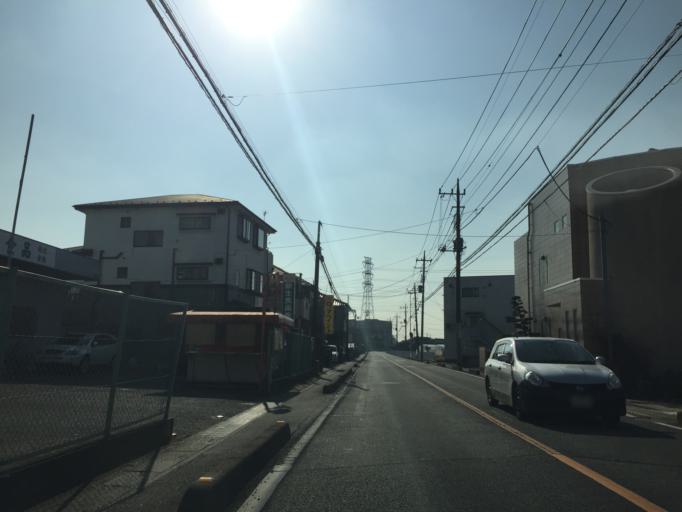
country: JP
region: Saitama
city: Shiki
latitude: 35.8445
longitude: 139.5822
